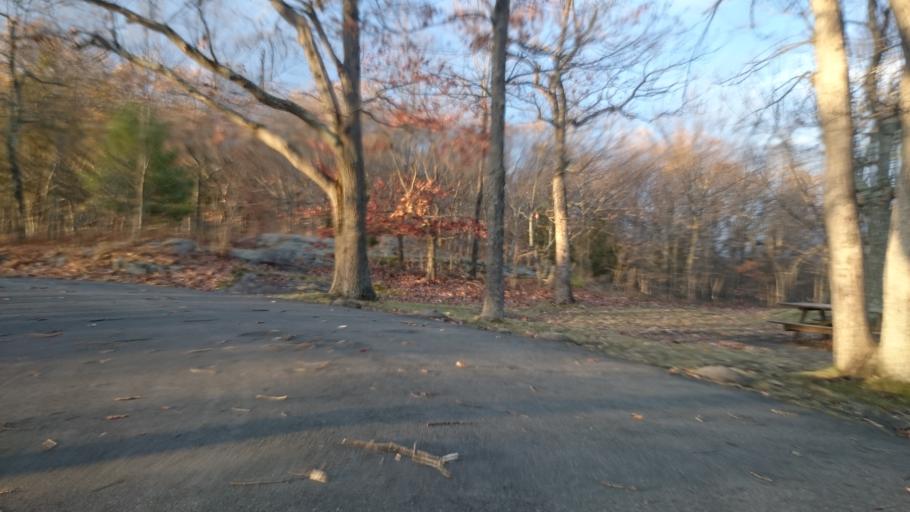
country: US
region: Connecticut
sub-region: New Haven County
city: Woodbridge
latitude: 41.3385
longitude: -72.9666
